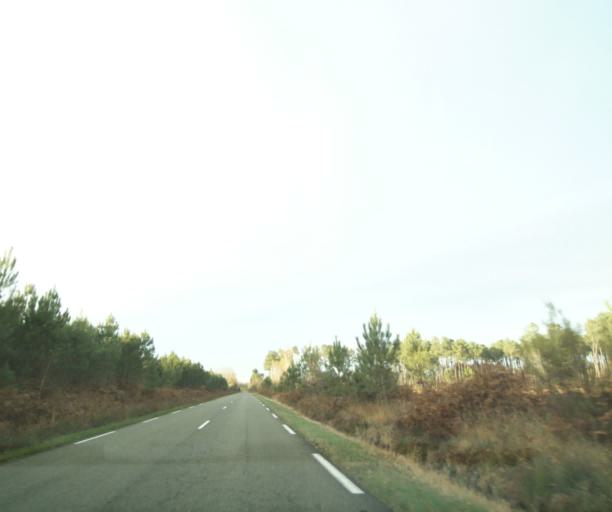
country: FR
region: Aquitaine
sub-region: Departement des Landes
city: Gabarret
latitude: 44.0919
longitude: -0.0970
